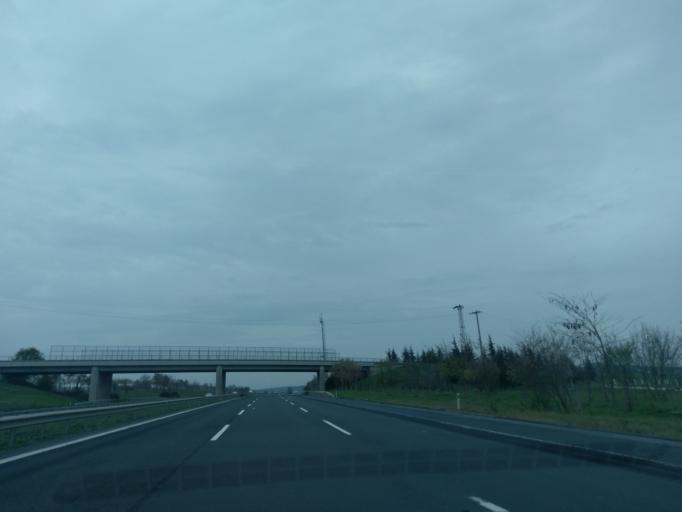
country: TR
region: Istanbul
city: Canta
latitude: 41.1398
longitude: 28.1500
